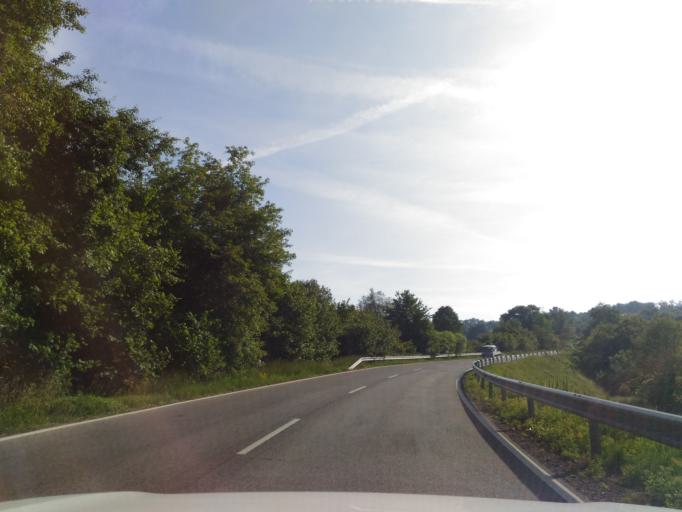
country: HU
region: Baranya
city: Komlo
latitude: 46.1673
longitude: 18.2550
